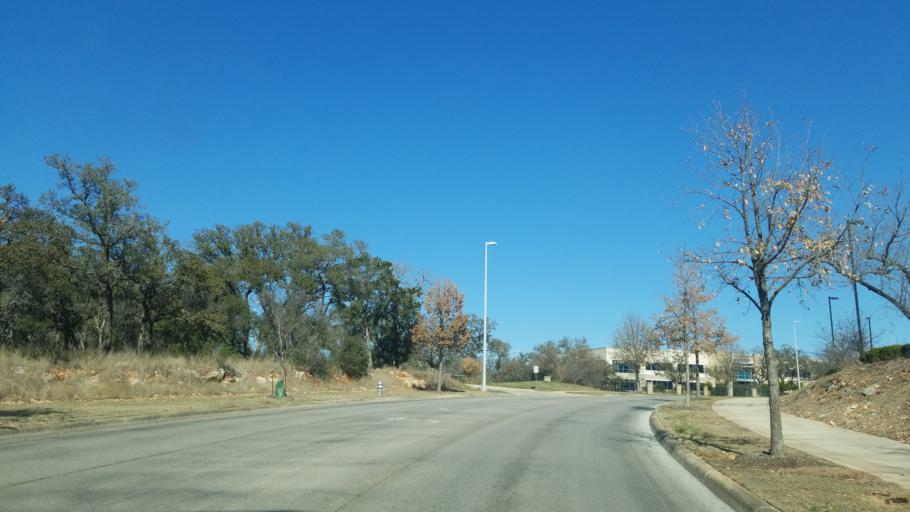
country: US
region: Texas
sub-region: Bexar County
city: Hollywood Park
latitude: 29.6187
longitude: -98.4608
